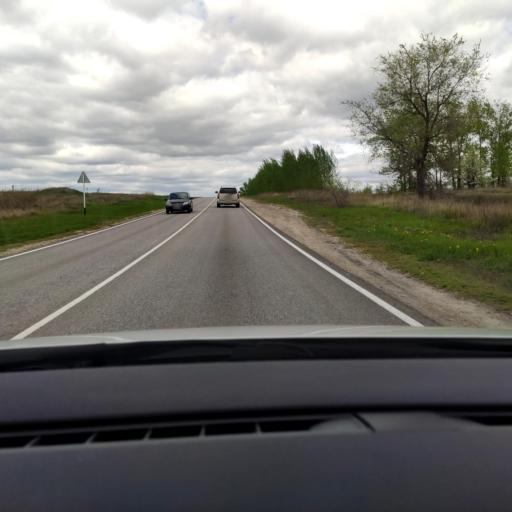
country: RU
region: Voronezj
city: Volya
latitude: 51.7186
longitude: 39.5408
